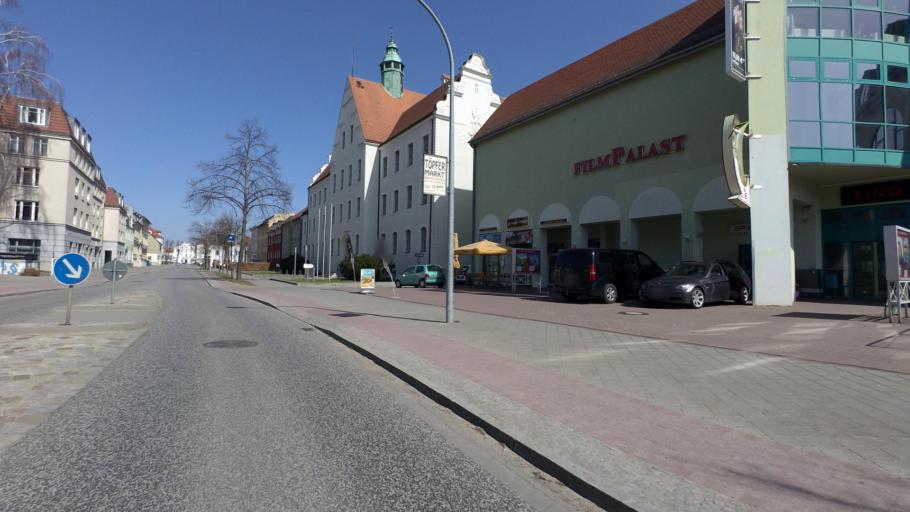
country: DE
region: Brandenburg
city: Oranienburg
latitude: 52.7499
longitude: 13.2372
